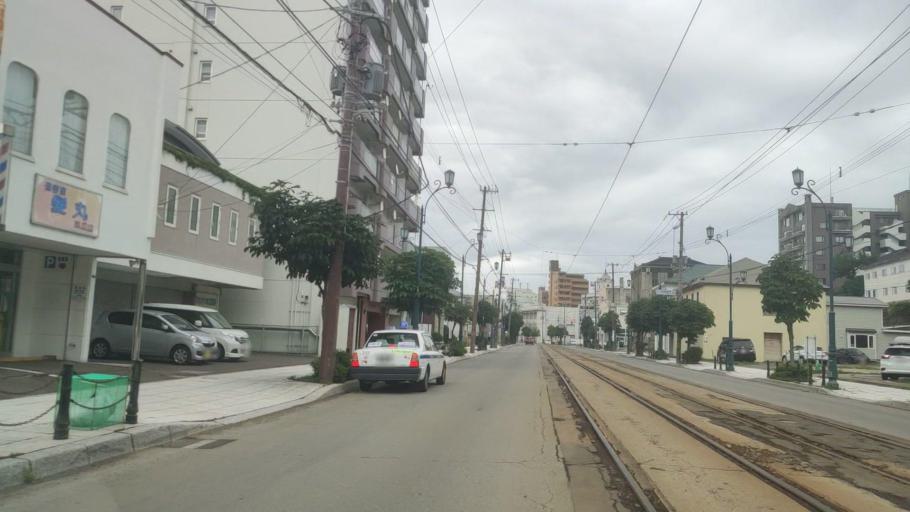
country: JP
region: Hokkaido
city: Hakodate
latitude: 41.7654
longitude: 140.7144
